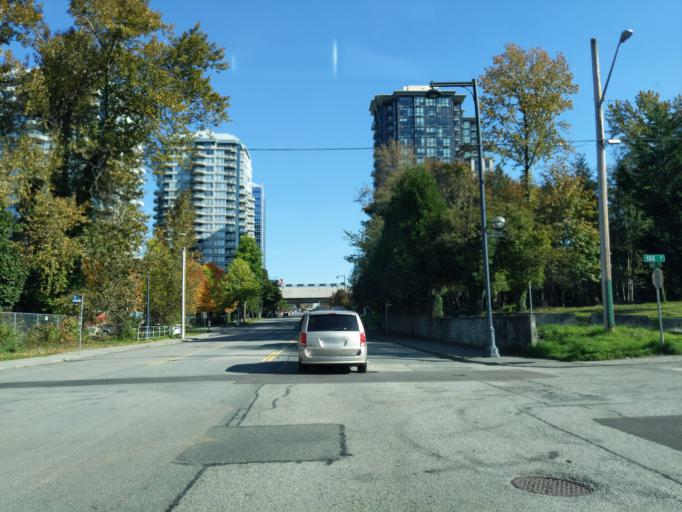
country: CA
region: British Columbia
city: New Westminster
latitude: 49.1989
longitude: -122.8540
